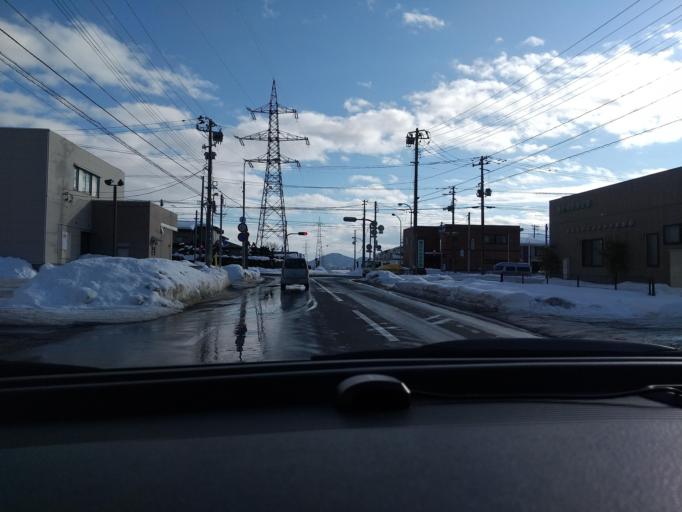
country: JP
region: Iwate
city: Morioka-shi
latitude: 39.7320
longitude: 141.0892
